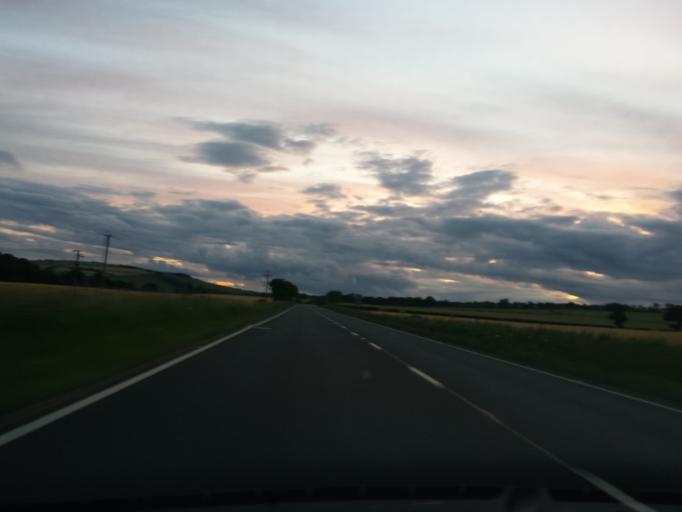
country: GB
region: Scotland
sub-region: The Scottish Borders
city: Chirnside
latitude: 55.8562
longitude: -2.2037
